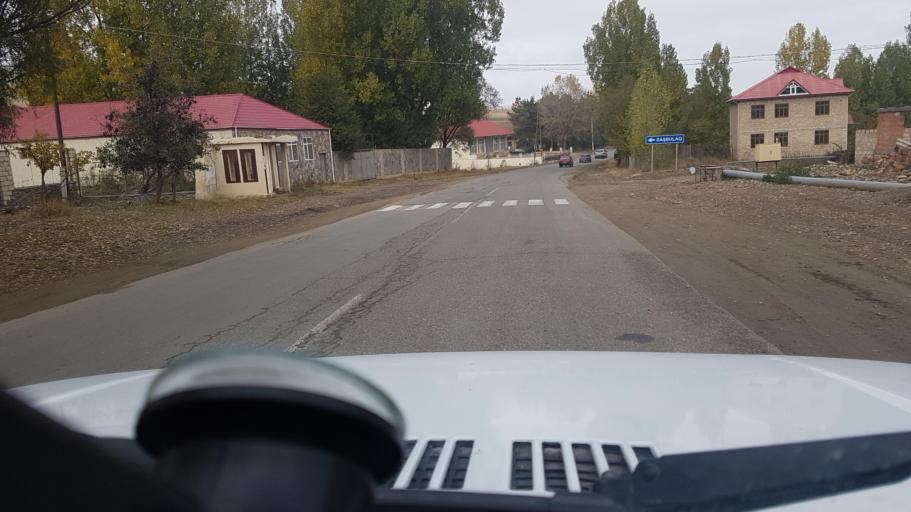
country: AZ
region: Gadabay Rayon
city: Ariqdam
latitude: 40.6330
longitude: 45.8135
